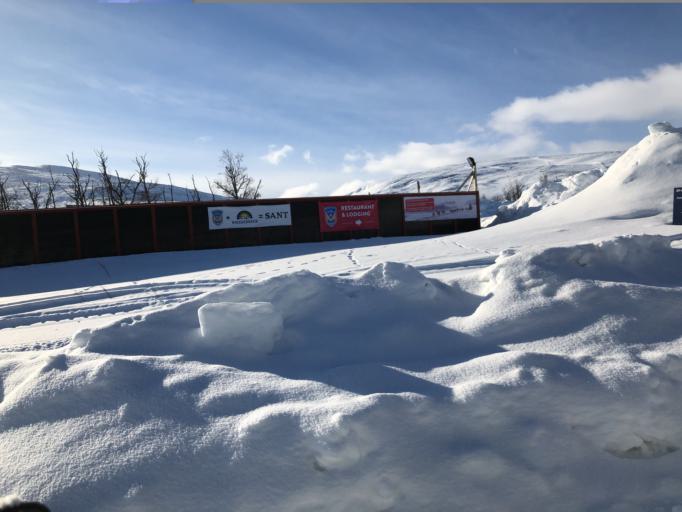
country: NO
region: Troms
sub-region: Bardu
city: Setermoen
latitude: 68.4103
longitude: 18.6810
